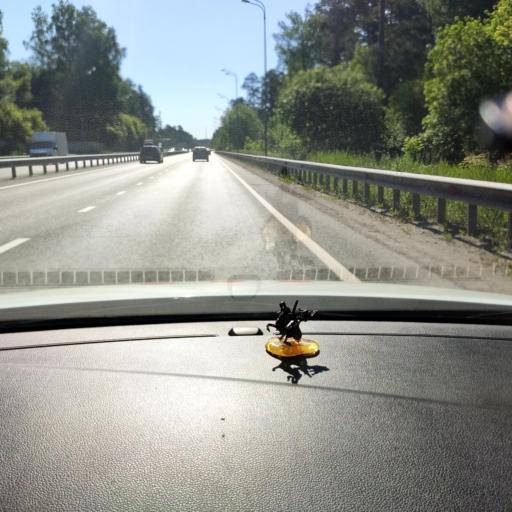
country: RU
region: Tatarstan
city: Staroye Arakchino
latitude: 55.8396
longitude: 48.9586
